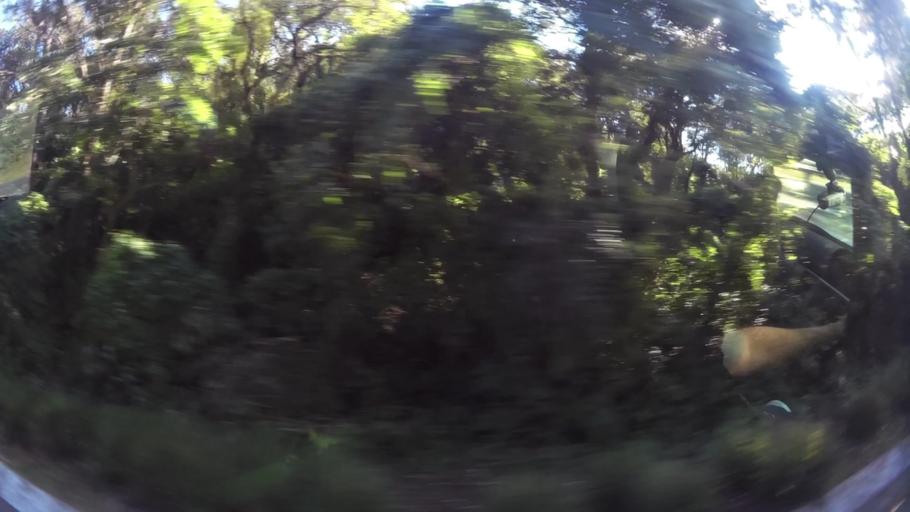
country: GT
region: Sacatepequez
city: Antigua Guatemala
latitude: 14.5607
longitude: -90.7101
